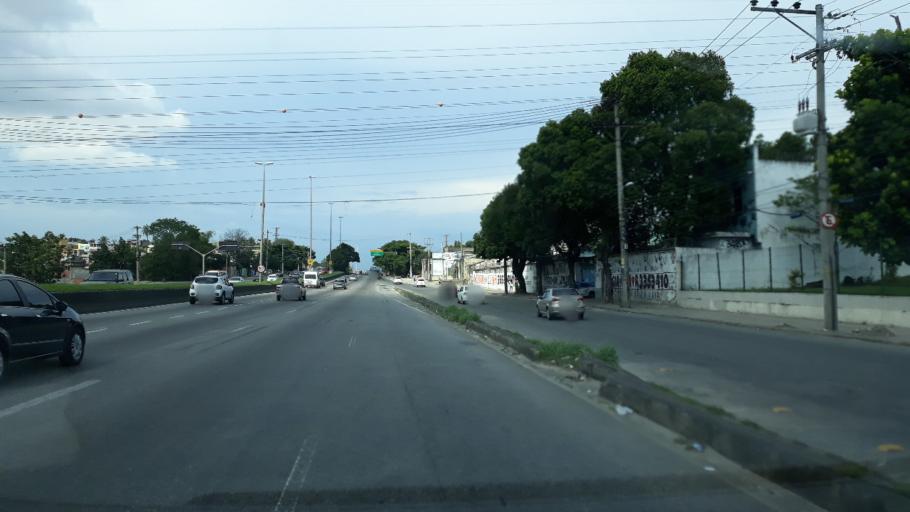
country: BR
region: Rio de Janeiro
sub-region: Sao Joao De Meriti
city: Sao Joao de Meriti
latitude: -22.8398
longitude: -43.3685
